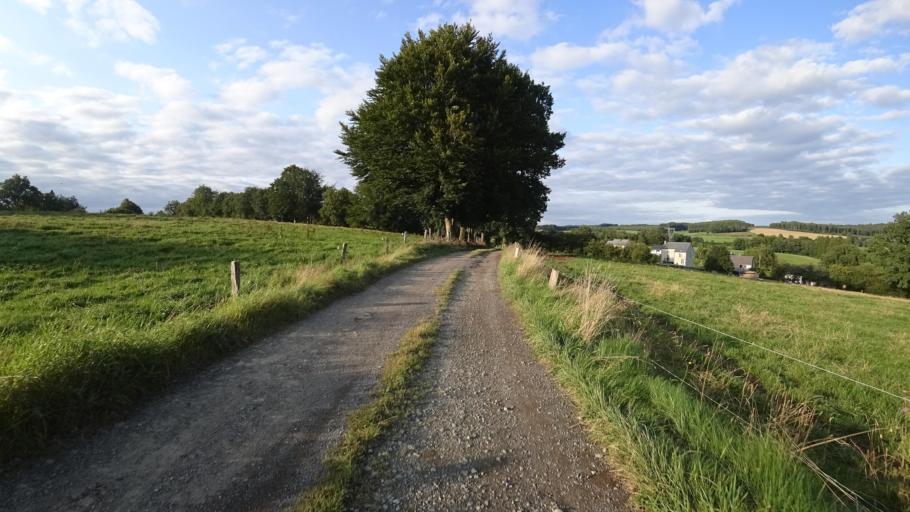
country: BE
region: Wallonia
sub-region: Province du Luxembourg
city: Neufchateau
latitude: 49.8635
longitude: 5.3704
